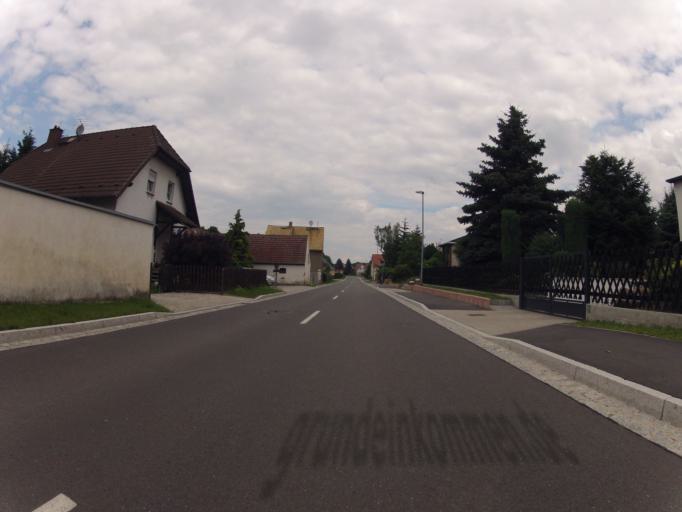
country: DE
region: Saxony
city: Schildau
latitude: 51.4457
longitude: 12.9302
